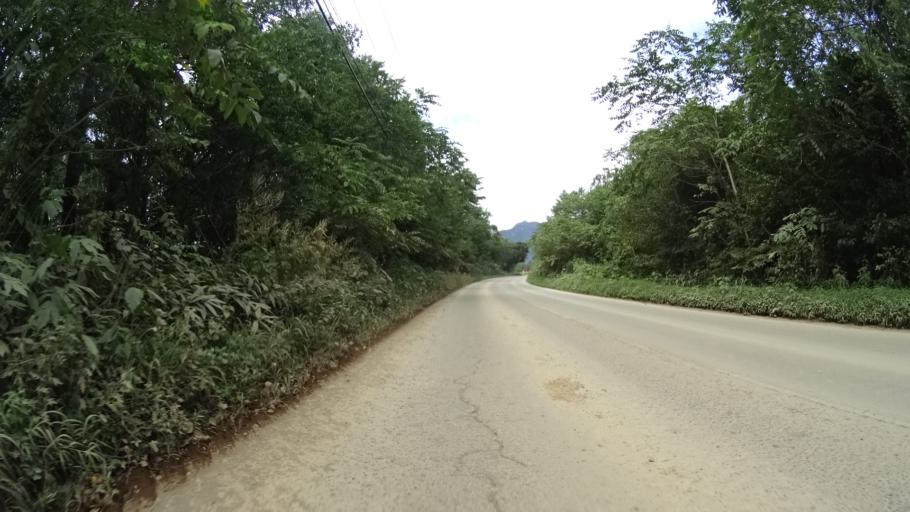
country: JP
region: Yamanashi
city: Nirasaki
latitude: 35.9465
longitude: 138.5477
